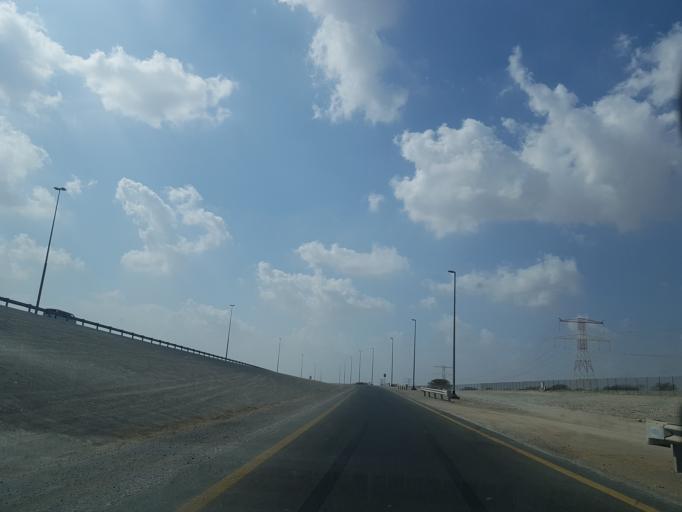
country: AE
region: Ra's al Khaymah
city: Ras al-Khaimah
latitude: 25.7625
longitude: 56.0217
